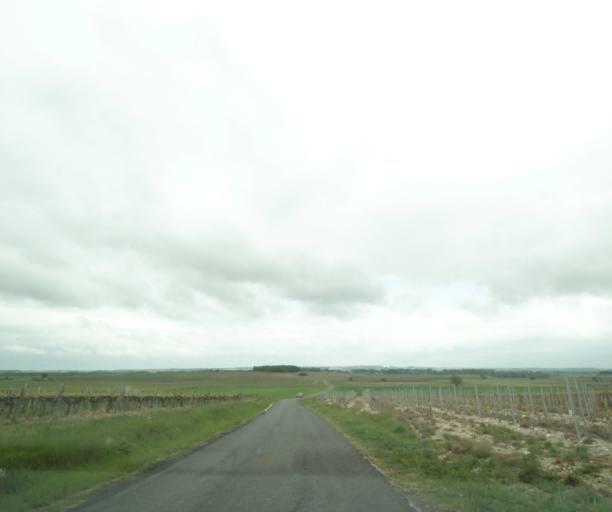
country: FR
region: Poitou-Charentes
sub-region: Departement de la Charente-Maritime
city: Perignac
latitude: 45.6655
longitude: -0.5003
